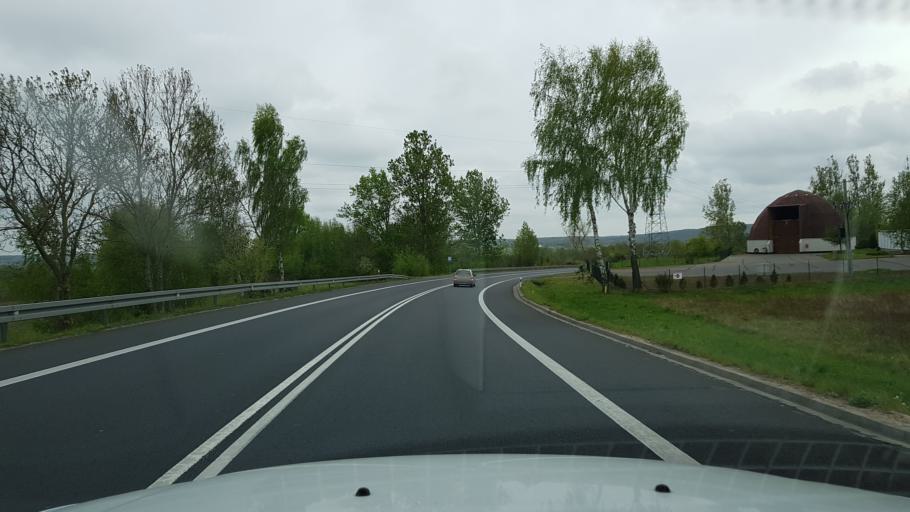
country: PL
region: West Pomeranian Voivodeship
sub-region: Powiat slawienski
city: Darlowo
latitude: 54.3007
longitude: 16.5081
